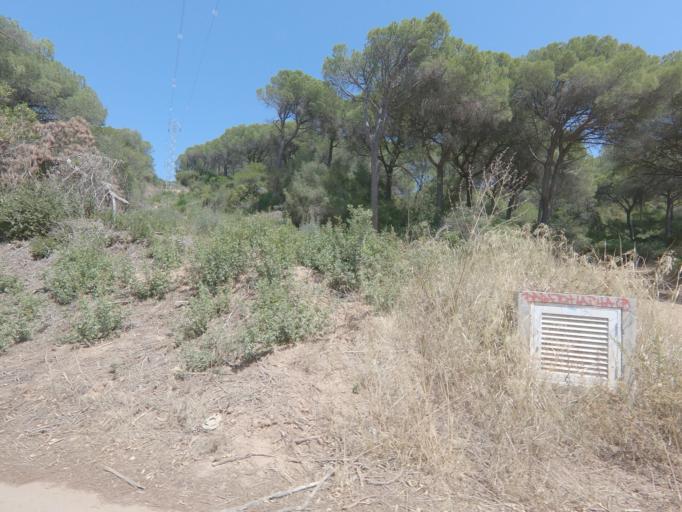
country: PT
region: Setubal
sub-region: Setubal
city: Setubal
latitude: 38.5119
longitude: -8.9293
